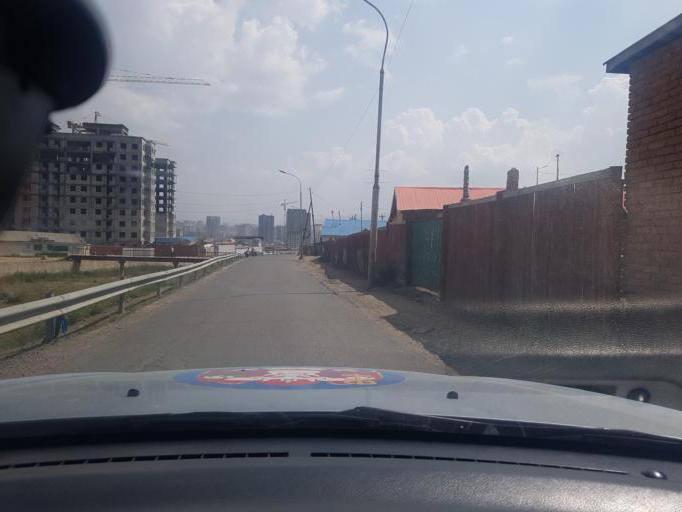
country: MN
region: Ulaanbaatar
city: Ulaanbaatar
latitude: 47.9381
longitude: 106.8985
